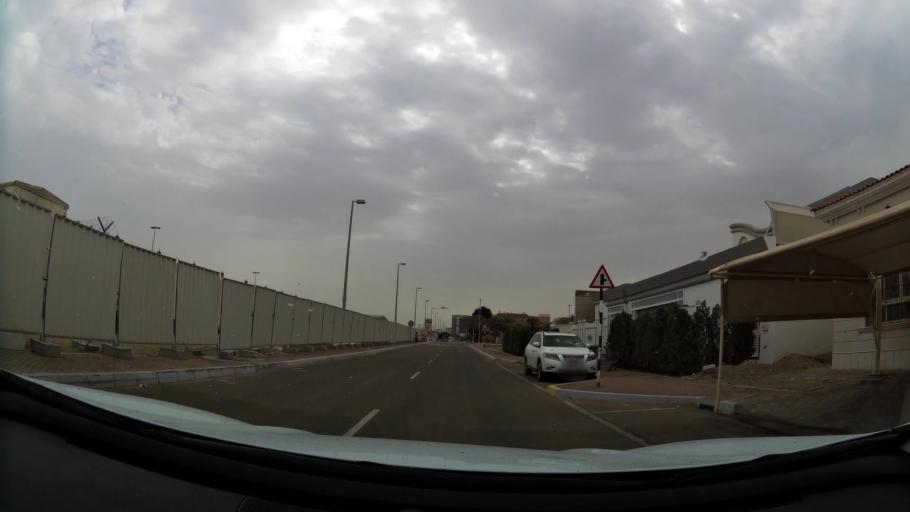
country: AE
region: Abu Dhabi
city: Abu Dhabi
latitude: 24.4303
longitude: 54.4474
